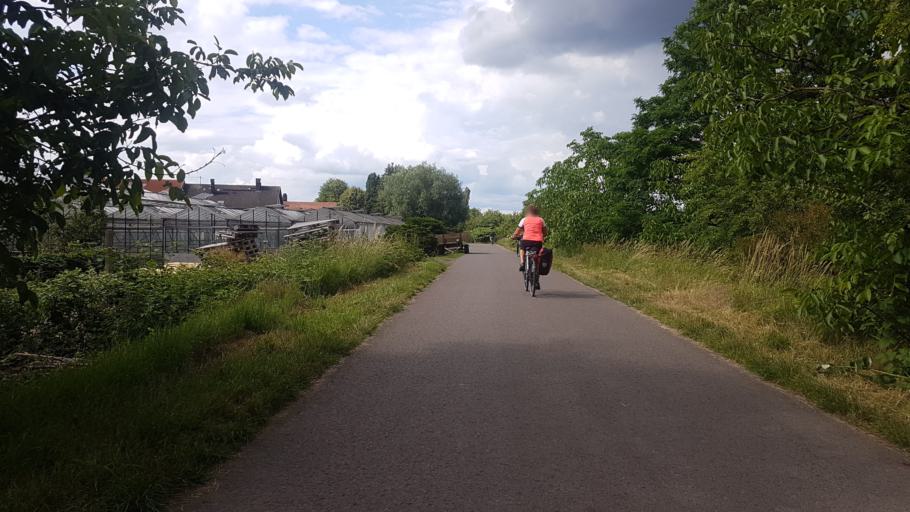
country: DE
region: Saarland
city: Ensdorf
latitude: 49.2994
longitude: 6.7645
